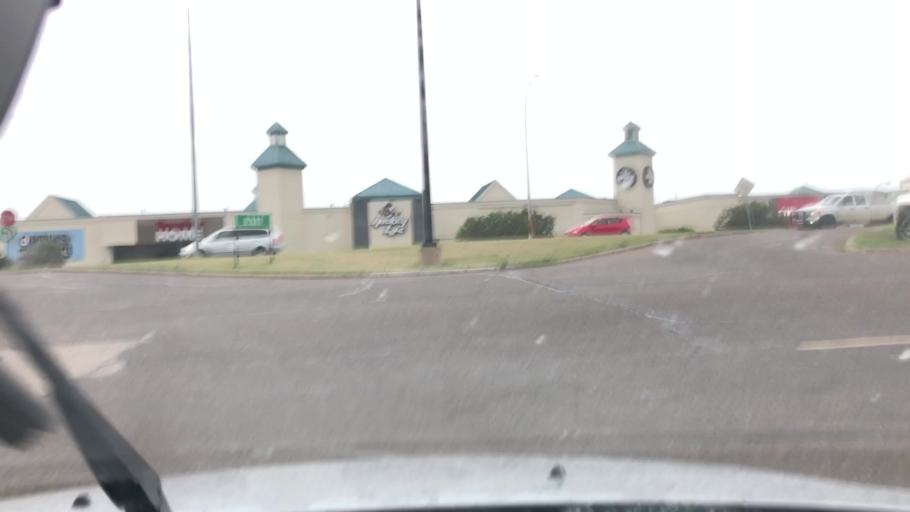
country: CA
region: Alberta
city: St. Albert
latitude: 53.5423
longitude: -113.6156
